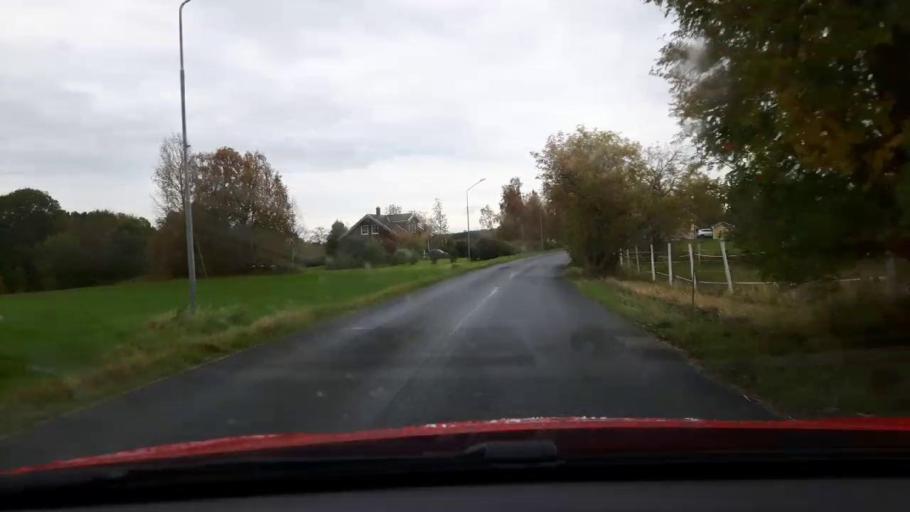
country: SE
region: Jaemtland
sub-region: Bergs Kommun
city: Hoverberg
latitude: 62.9189
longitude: 14.5190
